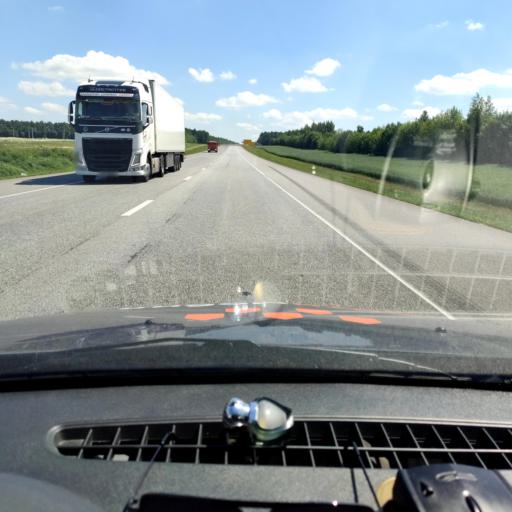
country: RU
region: Orjol
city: Zmiyevka
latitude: 52.8093
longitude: 36.2927
